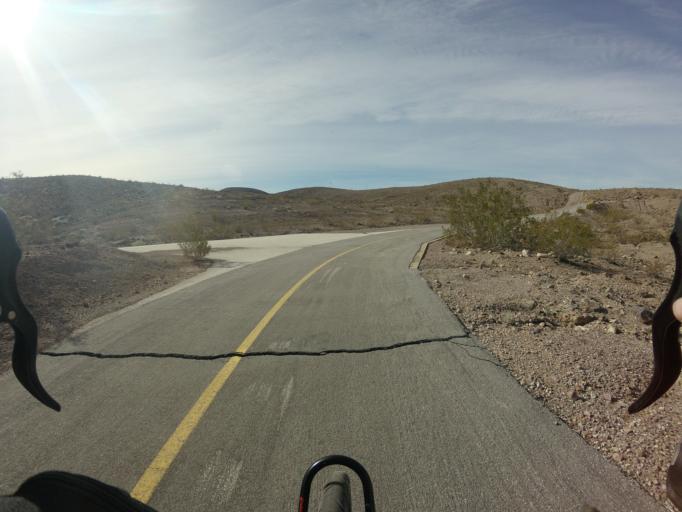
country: US
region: Nevada
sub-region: Clark County
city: Henderson
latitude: 36.1104
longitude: -114.8769
